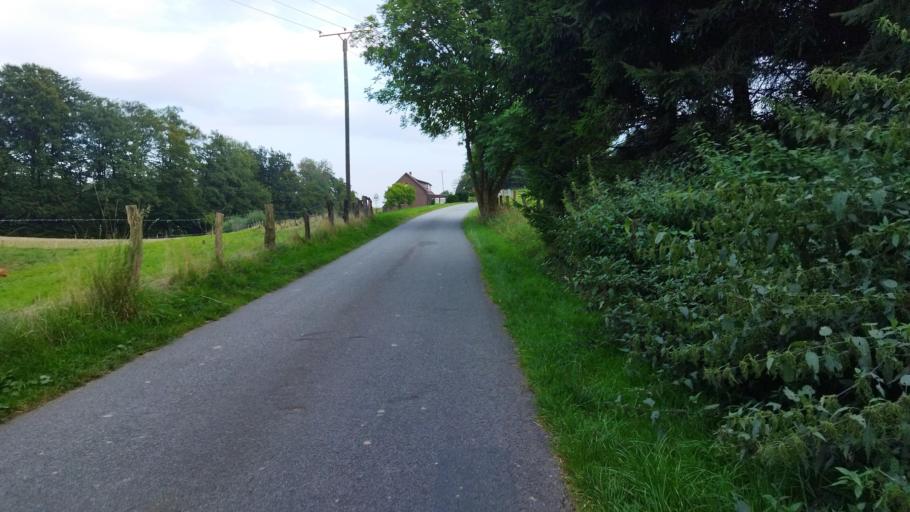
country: DE
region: Lower Saxony
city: Hagen
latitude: 52.1788
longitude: 8.0064
